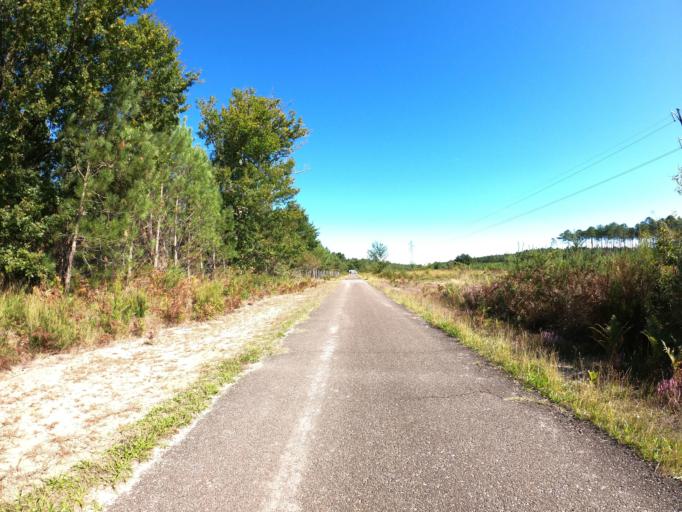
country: FR
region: Aquitaine
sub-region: Departement des Landes
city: Ychoux
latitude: 44.3405
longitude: -0.9720
